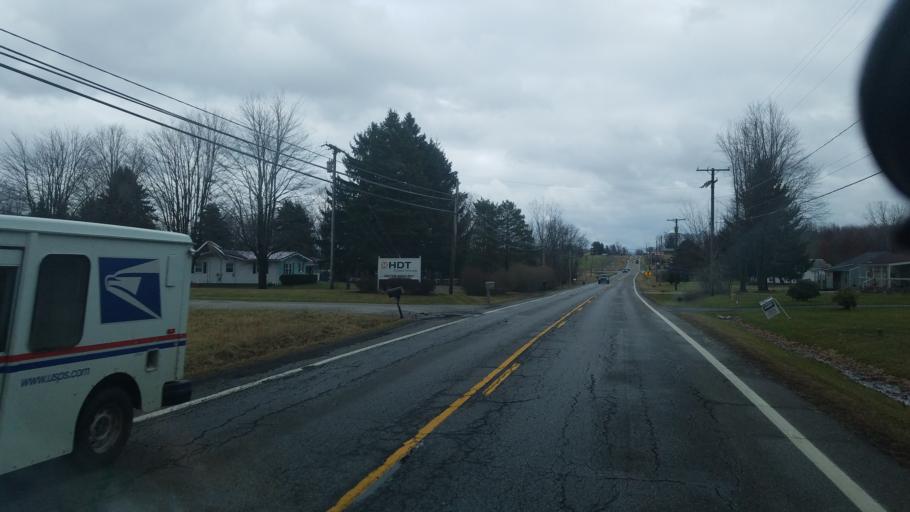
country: US
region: Ohio
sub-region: Richland County
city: Ontario
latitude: 40.7646
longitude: -82.6622
